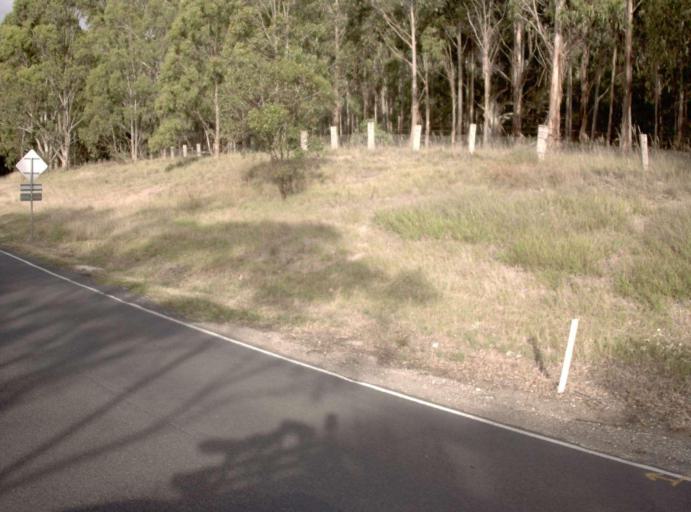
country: AU
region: Victoria
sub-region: Wellington
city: Sale
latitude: -37.9269
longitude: 146.9928
